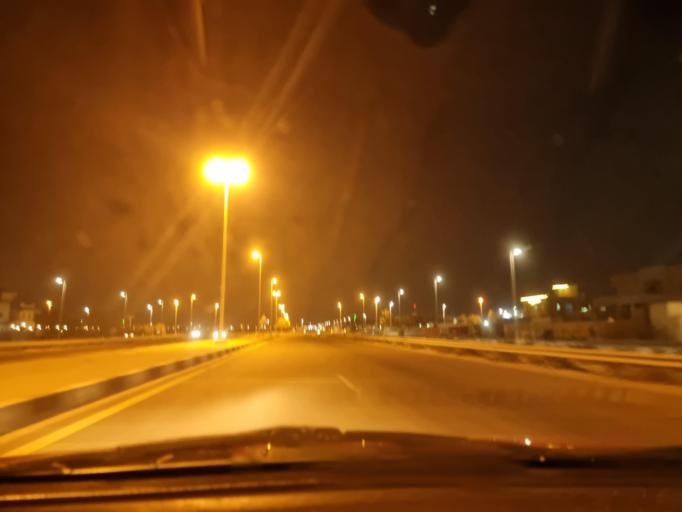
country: AE
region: Abu Dhabi
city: Abu Dhabi
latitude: 24.3667
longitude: 54.7047
